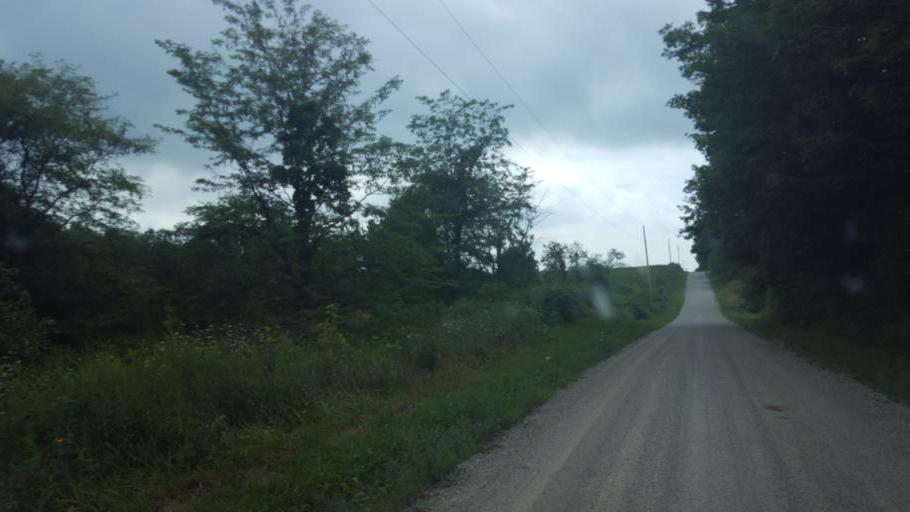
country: US
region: Ohio
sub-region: Morrow County
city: Mount Gilead
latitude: 40.5348
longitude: -82.6866
